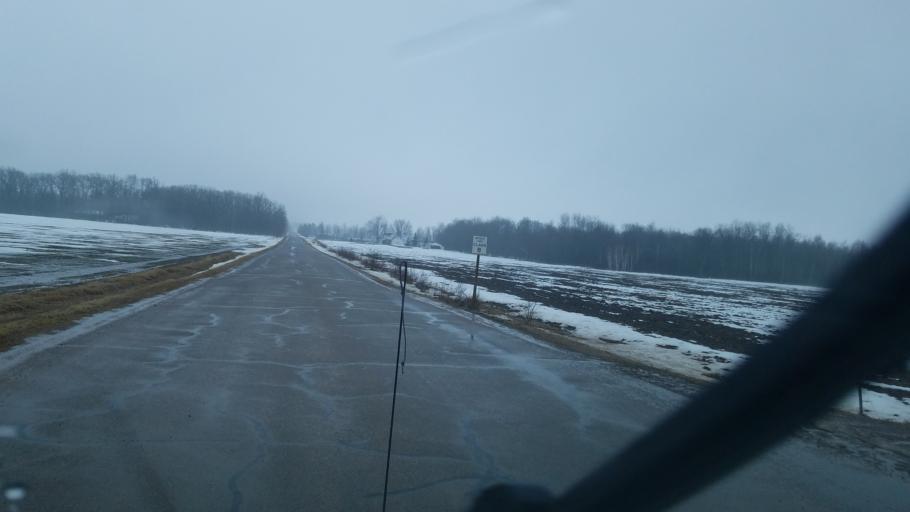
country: US
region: Wisconsin
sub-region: Marathon County
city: Spencer
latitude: 44.6775
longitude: -90.2793
